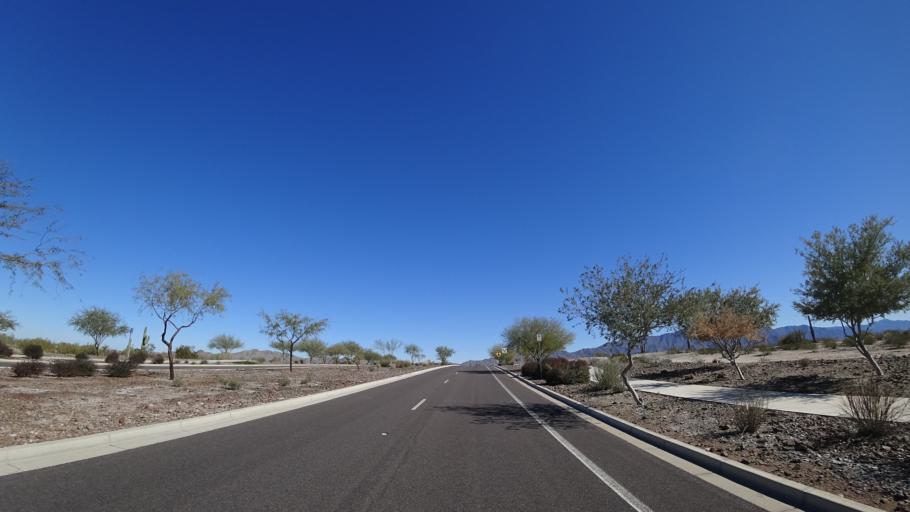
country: US
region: Arizona
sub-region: Maricopa County
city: Goodyear
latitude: 33.3061
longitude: -112.4350
